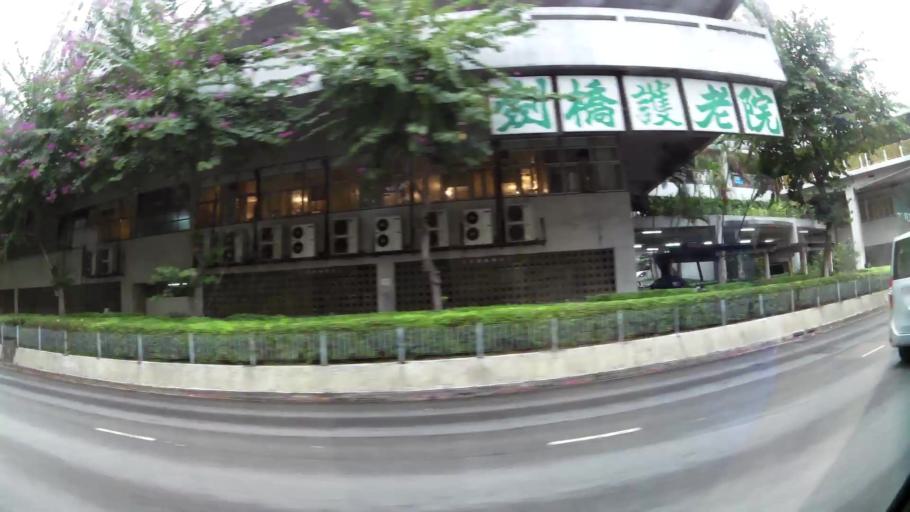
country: HK
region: Tsuen Wan
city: Tsuen Wan
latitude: 22.3703
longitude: 114.1206
